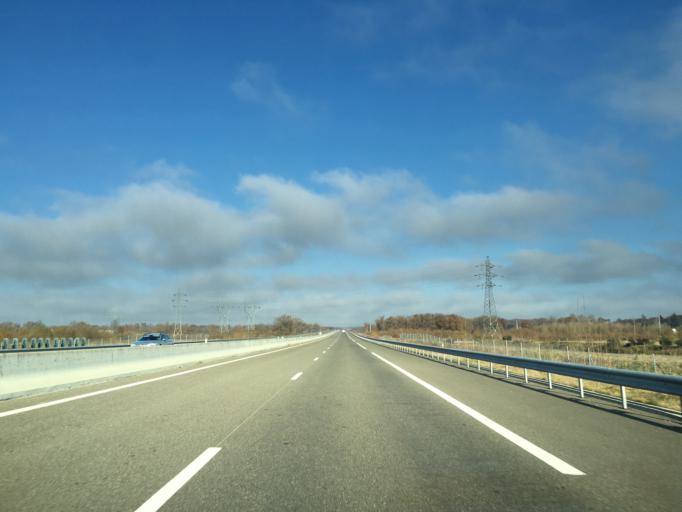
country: FR
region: Midi-Pyrenees
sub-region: Departement du Gers
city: Barcelonne-du-Gers
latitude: 43.7403
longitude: -0.2752
